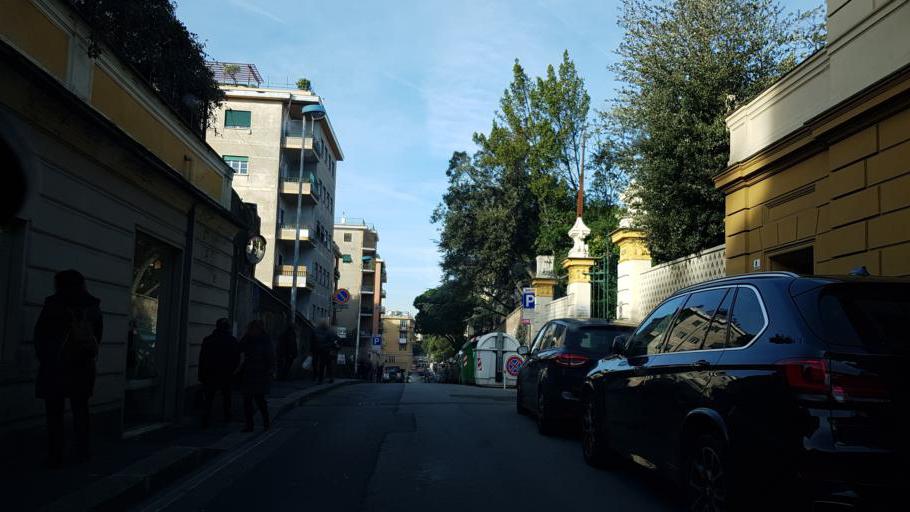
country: IT
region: Liguria
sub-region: Provincia di Genova
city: Genoa
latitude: 44.3982
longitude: 8.9663
